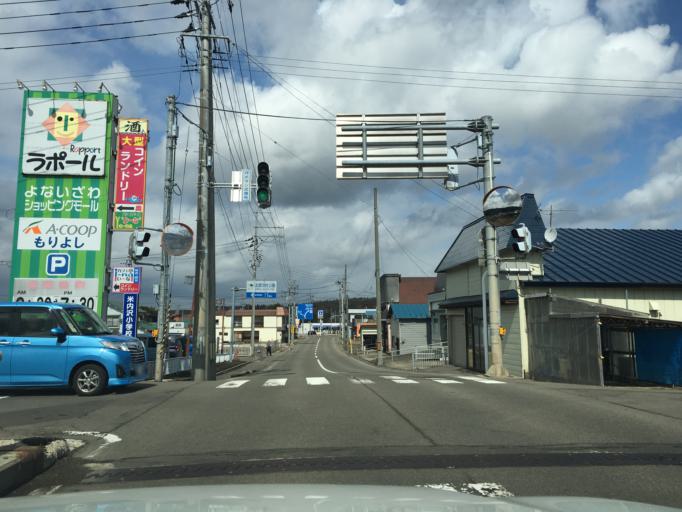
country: JP
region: Akita
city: Takanosu
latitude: 40.1219
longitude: 140.3673
